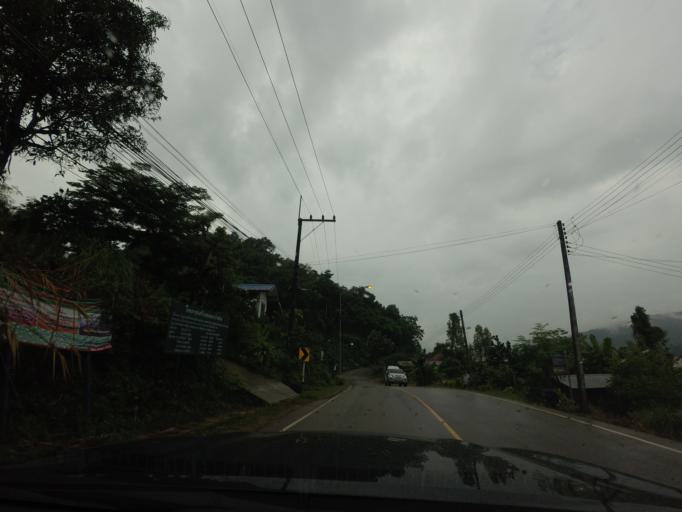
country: TH
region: Nong Khai
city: Sangkhom
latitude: 18.2072
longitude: 102.1278
